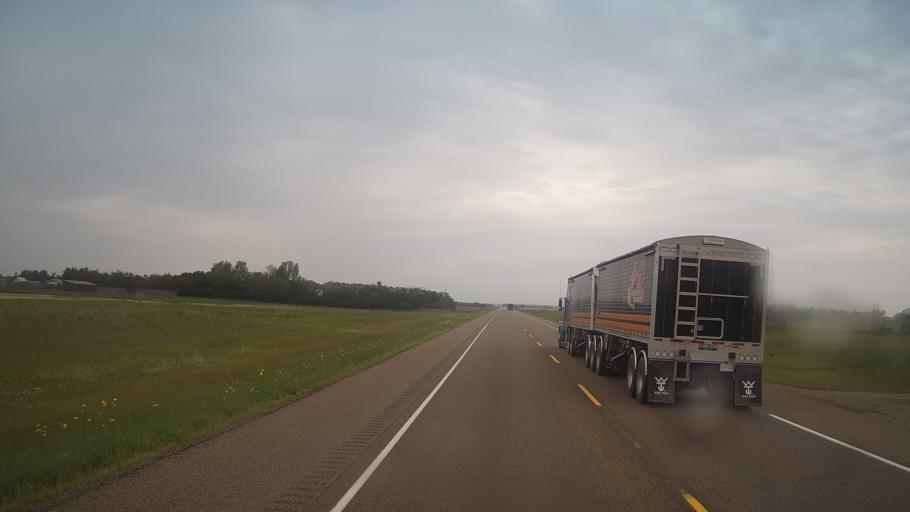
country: CA
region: Saskatchewan
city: Langham
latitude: 52.1293
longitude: -107.0633
